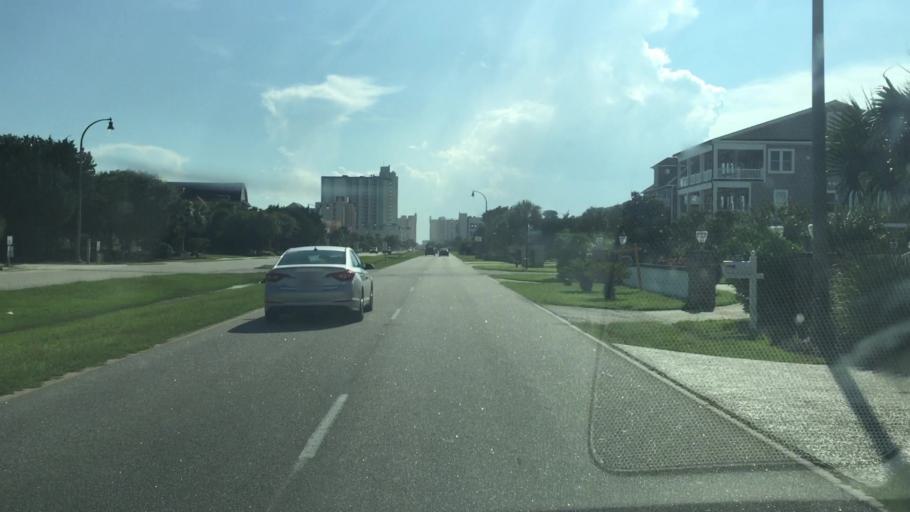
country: US
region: South Carolina
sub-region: Horry County
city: North Myrtle Beach
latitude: 33.8228
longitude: -78.6614
